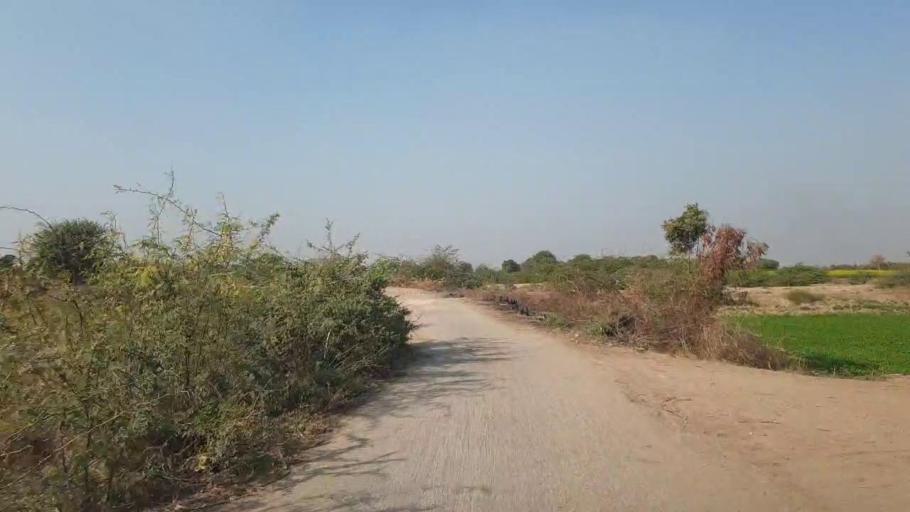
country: PK
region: Sindh
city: Mirpur Khas
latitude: 25.4169
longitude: 68.9178
